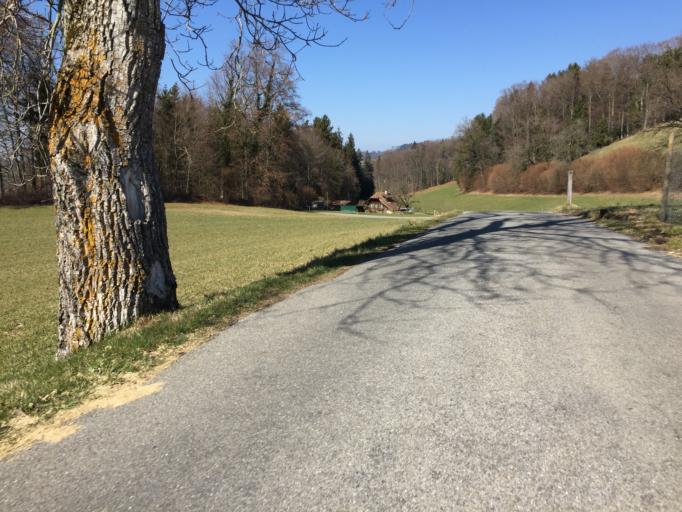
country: CH
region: Bern
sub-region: Bern-Mittelland District
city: Taegertschi
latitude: 46.9016
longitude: 7.5868
